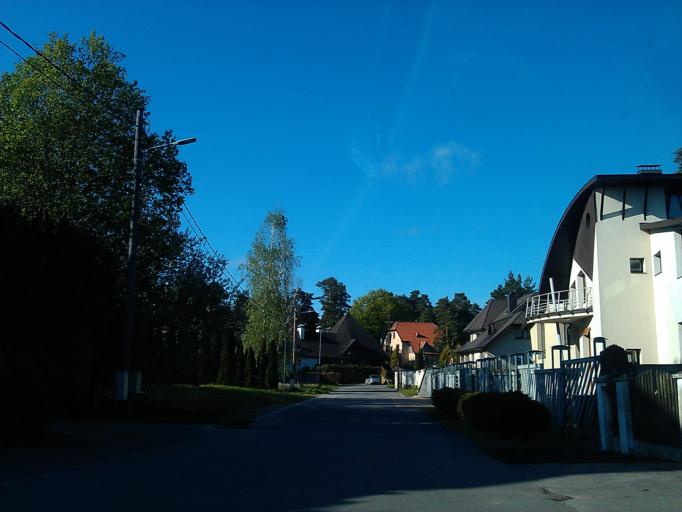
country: LV
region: Riga
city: Bergi
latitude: 57.0141
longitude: 24.2708
